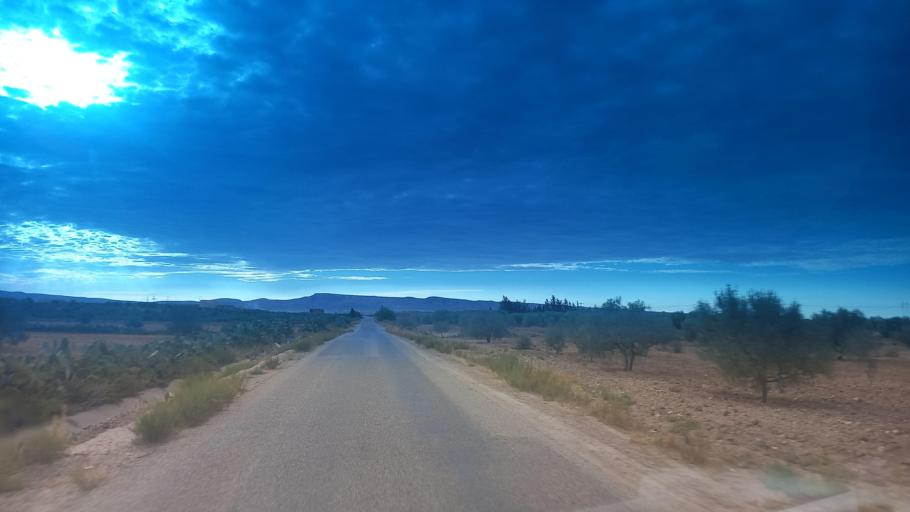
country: TN
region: Al Qasrayn
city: Sbiba
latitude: 35.3851
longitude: 9.0356
